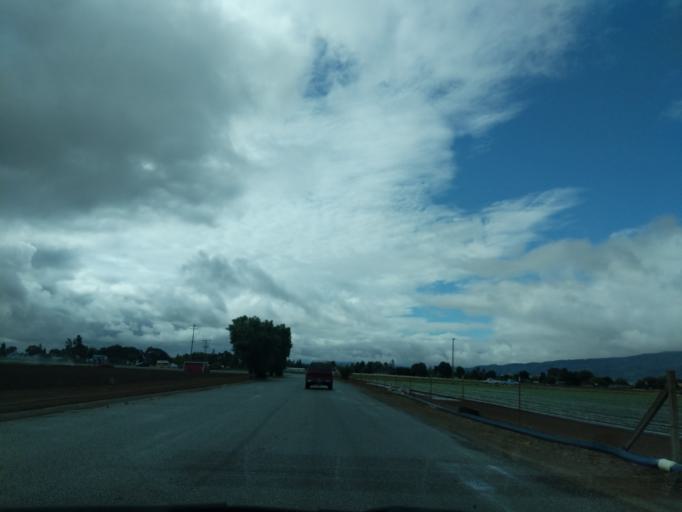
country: US
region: California
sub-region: Santa Clara County
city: San Martin
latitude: 37.0587
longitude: -121.5915
